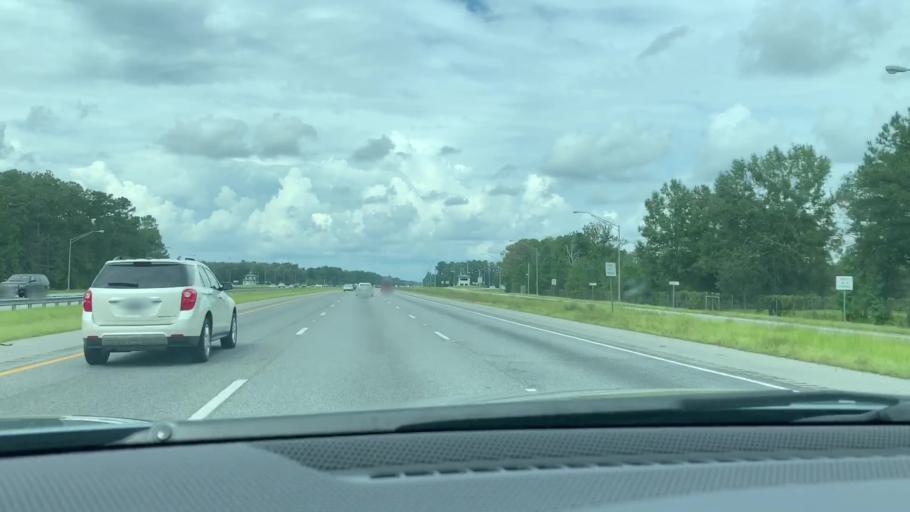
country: US
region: Georgia
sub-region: McIntosh County
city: Darien
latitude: 31.4730
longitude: -81.4469
